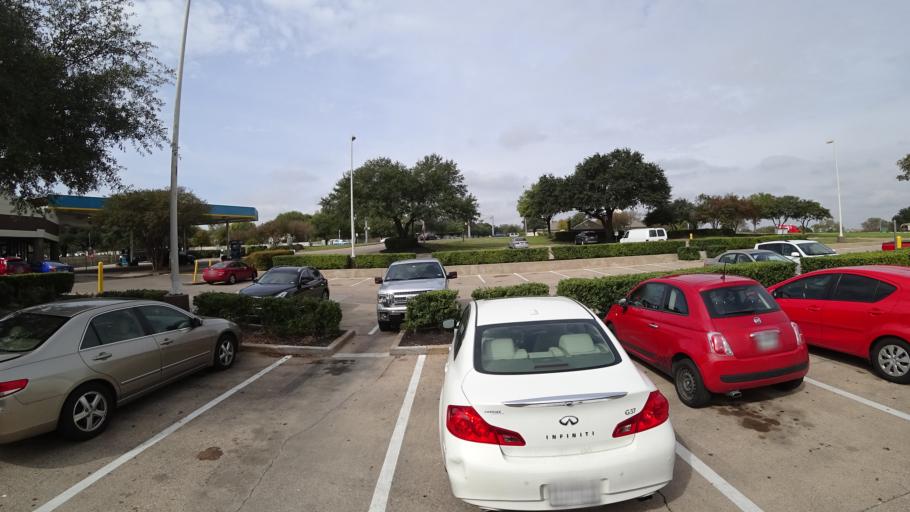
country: US
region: Texas
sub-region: Travis County
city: Wells Branch
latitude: 30.4354
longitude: -97.6743
